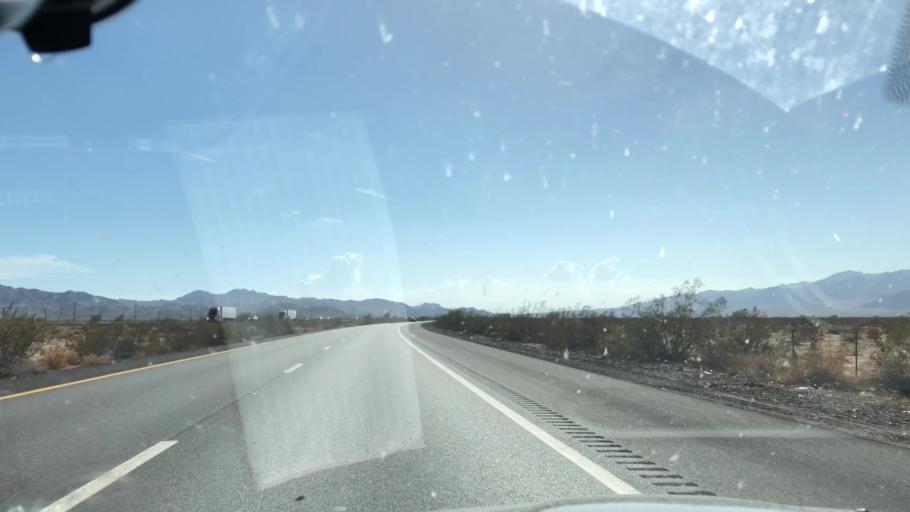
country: US
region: California
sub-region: Imperial County
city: Niland
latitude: 33.6744
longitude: -115.5787
